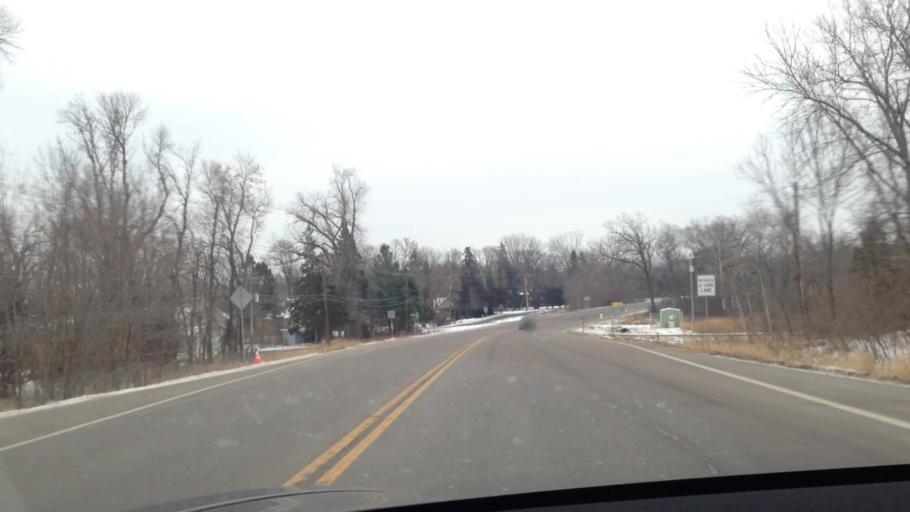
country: US
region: Minnesota
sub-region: Washington County
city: Forest Lake
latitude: 45.2623
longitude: -92.9477
